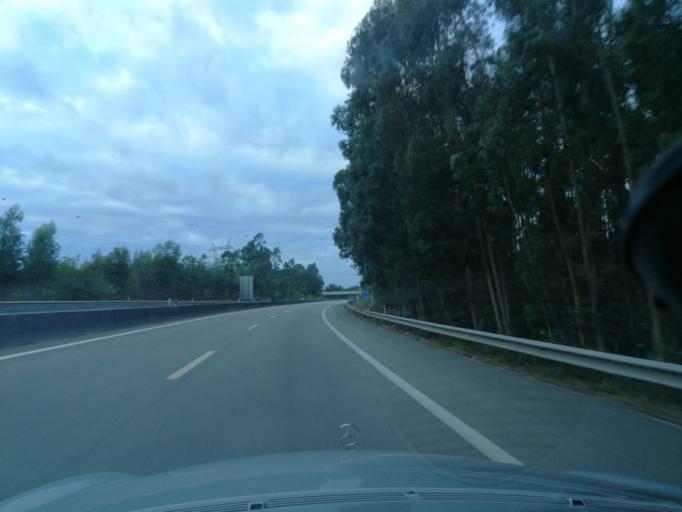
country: PT
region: Aveiro
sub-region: Albergaria-A-Velha
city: Albergaria-a-Velha
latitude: 40.6823
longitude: -8.4965
